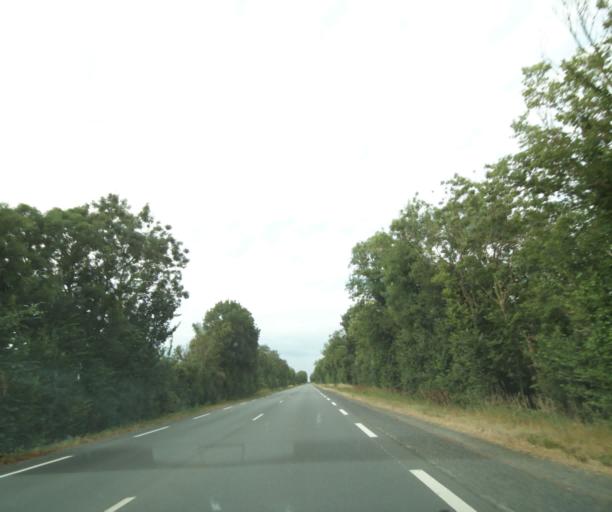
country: FR
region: Poitou-Charentes
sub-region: Departement de la Charente-Maritime
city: Andilly
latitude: 46.2705
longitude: -1.0039
